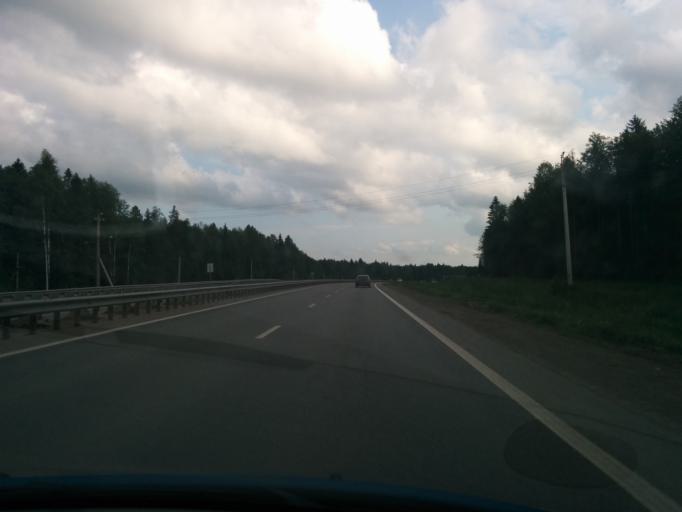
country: RU
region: Perm
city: Novyye Lyady
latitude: 58.0368
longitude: 56.4335
